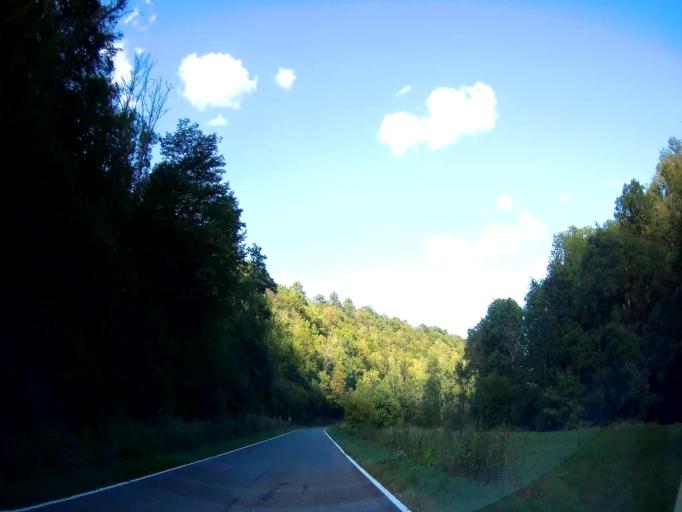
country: BE
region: Wallonia
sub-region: Province de Namur
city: Anhee
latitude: 50.3020
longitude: 4.8204
